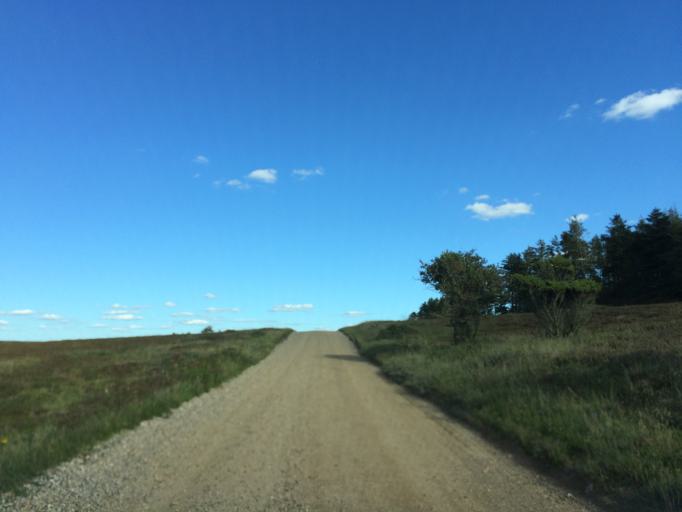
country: DK
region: Central Jutland
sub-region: Holstebro Kommune
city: Holstebro
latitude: 56.2769
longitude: 8.4875
